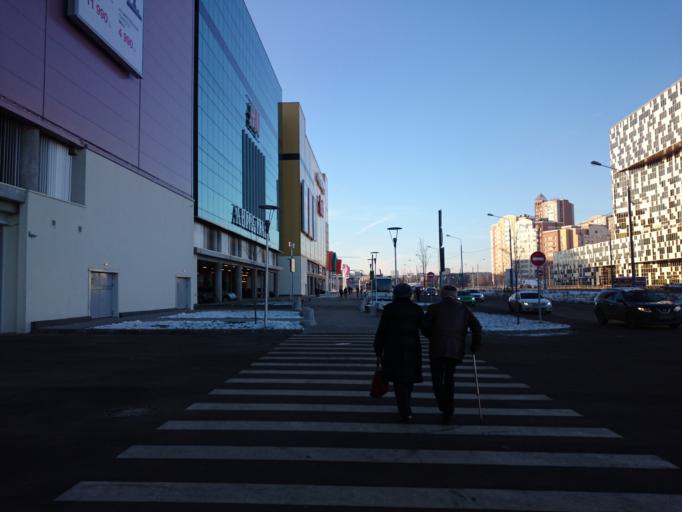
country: RU
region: Moscow
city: Sokol
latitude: 55.7912
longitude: 37.5304
